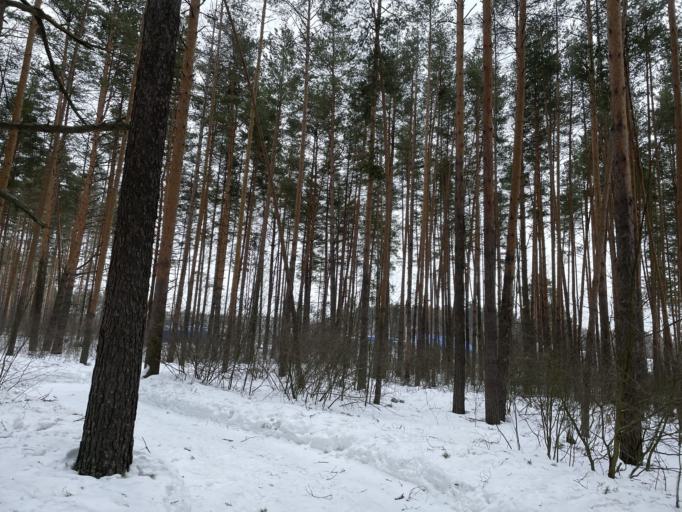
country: RU
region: Vladimir
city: Pokrov
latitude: 55.9378
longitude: 39.2375
